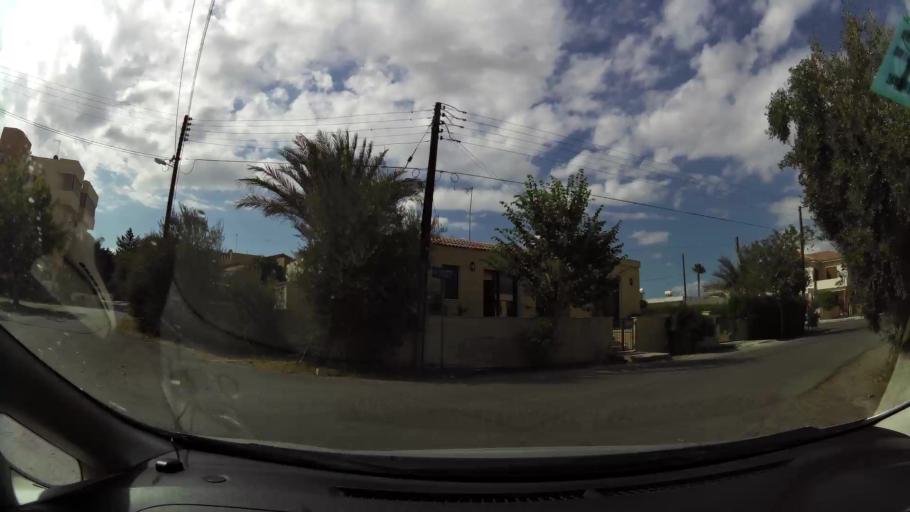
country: CY
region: Lefkosia
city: Nicosia
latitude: 35.1905
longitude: 33.3904
